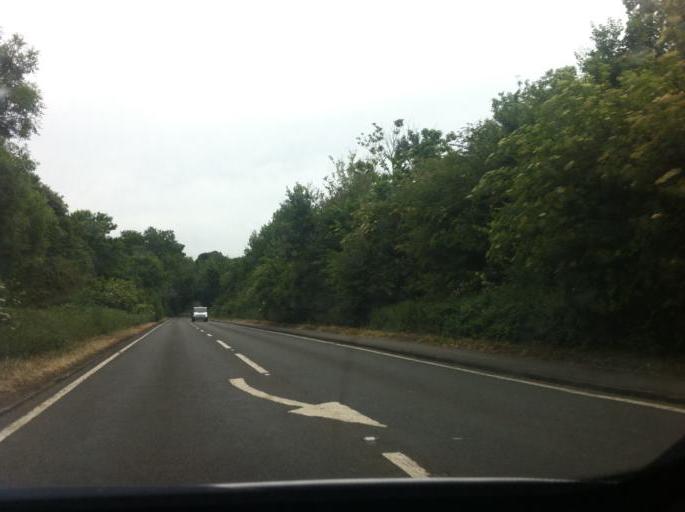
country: GB
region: England
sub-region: Northamptonshire
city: Earls Barton
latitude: 52.2639
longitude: -0.7986
